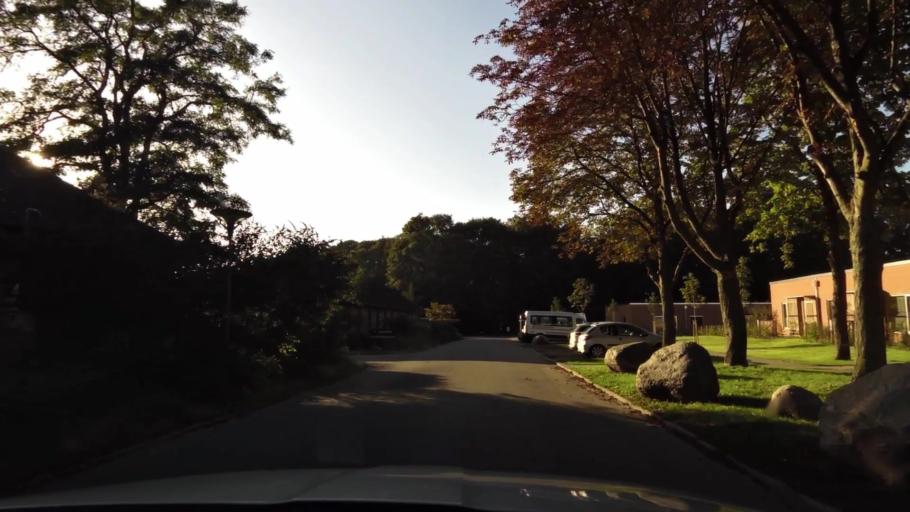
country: DK
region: Capital Region
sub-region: Lyngby-Tarbaek Kommune
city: Kongens Lyngby
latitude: 55.7522
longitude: 12.5085
